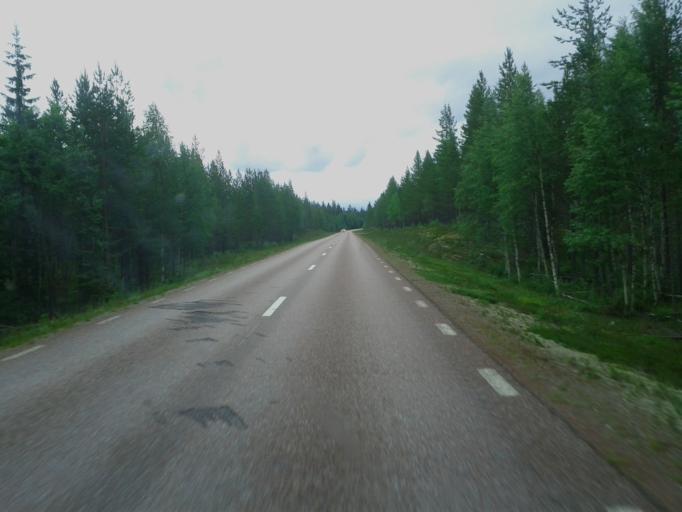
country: NO
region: Hedmark
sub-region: Trysil
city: Innbygda
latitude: 61.7066
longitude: 13.0180
